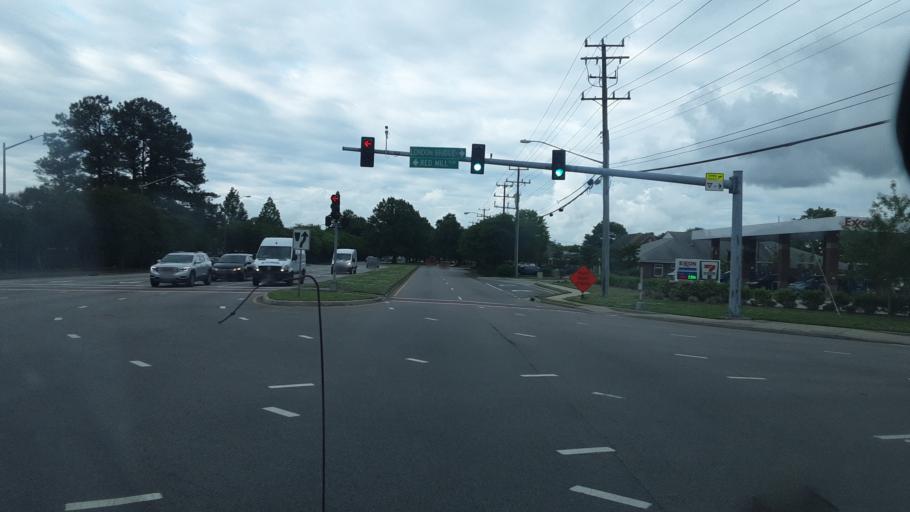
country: US
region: Virginia
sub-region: City of Virginia Beach
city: Virginia Beach
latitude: 36.7687
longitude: -76.0130
